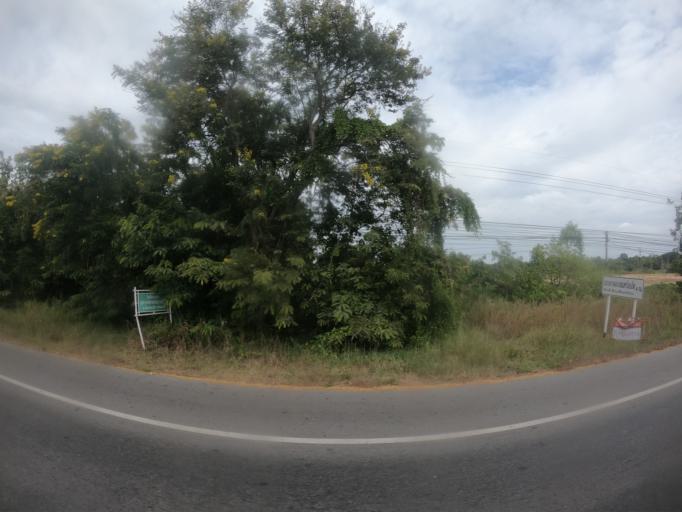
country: TH
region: Roi Et
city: Changhan
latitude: 16.0782
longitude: 103.5824
